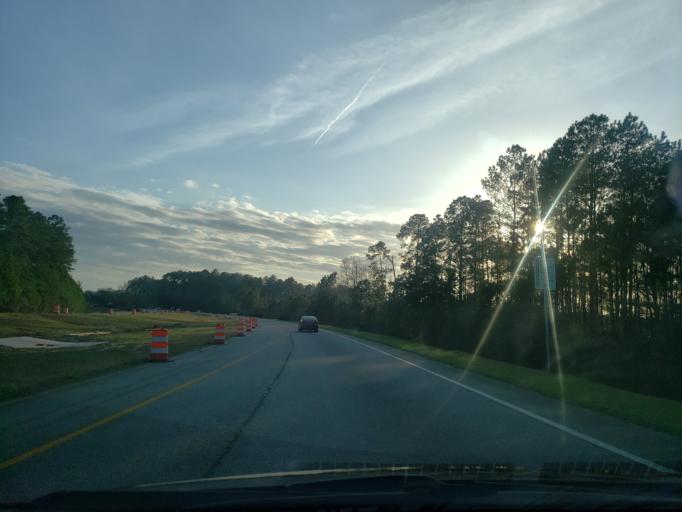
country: US
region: Georgia
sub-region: Chatham County
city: Bloomingdale
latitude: 32.1449
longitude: -81.3068
